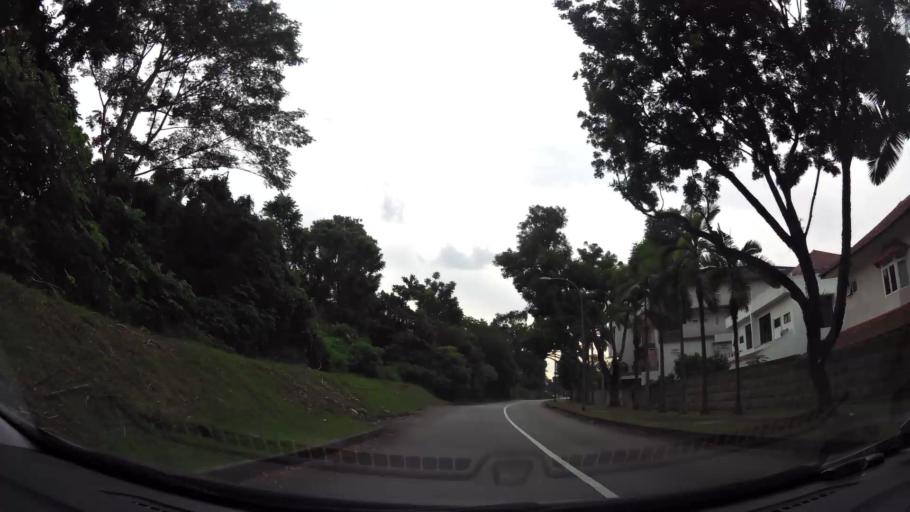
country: MY
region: Johor
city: Kampung Pasir Gudang Baru
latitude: 1.3979
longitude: 103.8256
